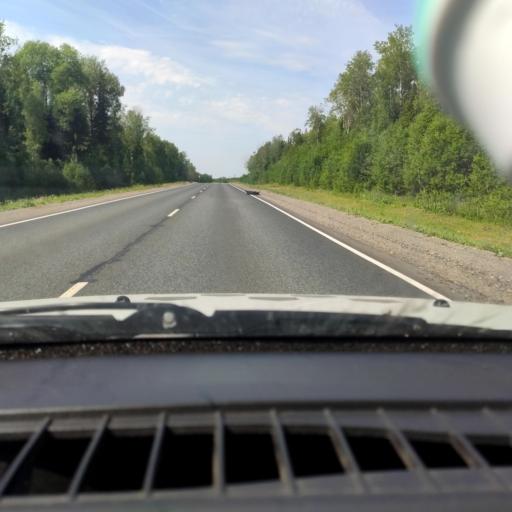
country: RU
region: Kirov
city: Kostino
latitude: 58.7463
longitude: 53.6153
